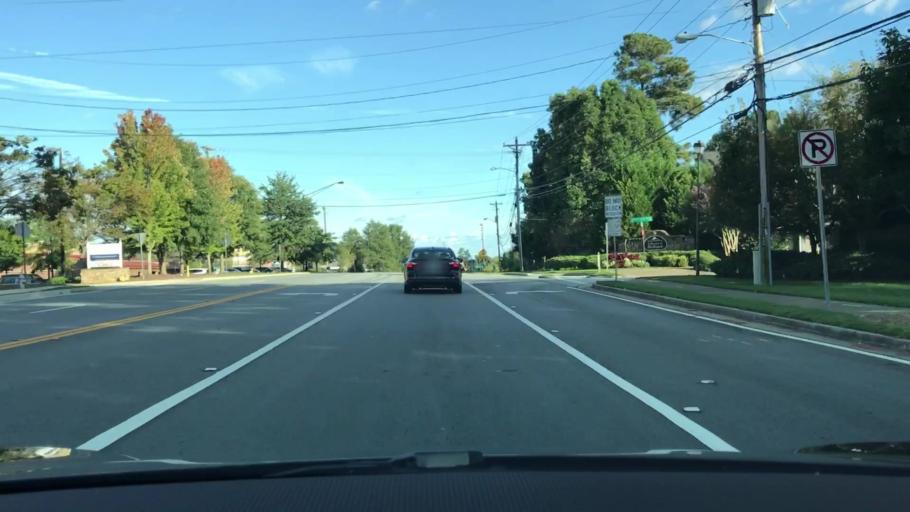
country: US
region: Georgia
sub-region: Gwinnett County
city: Dacula
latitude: 34.0376
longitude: -83.9128
